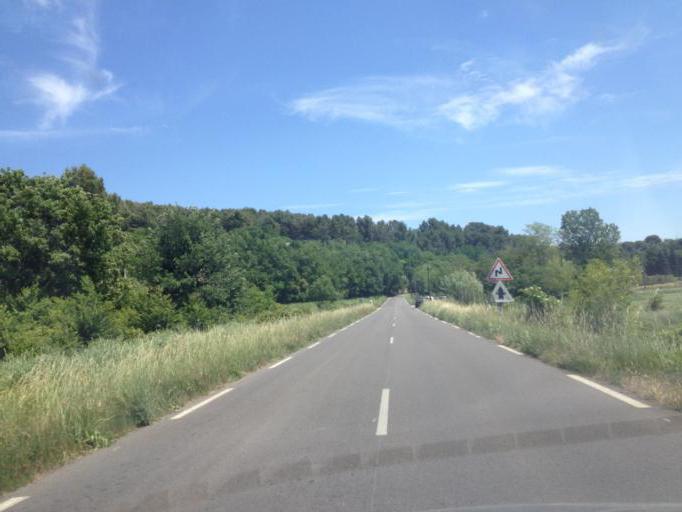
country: FR
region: Provence-Alpes-Cote d'Azur
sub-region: Departement du Vaucluse
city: Cadenet
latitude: 43.7408
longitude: 5.3467
